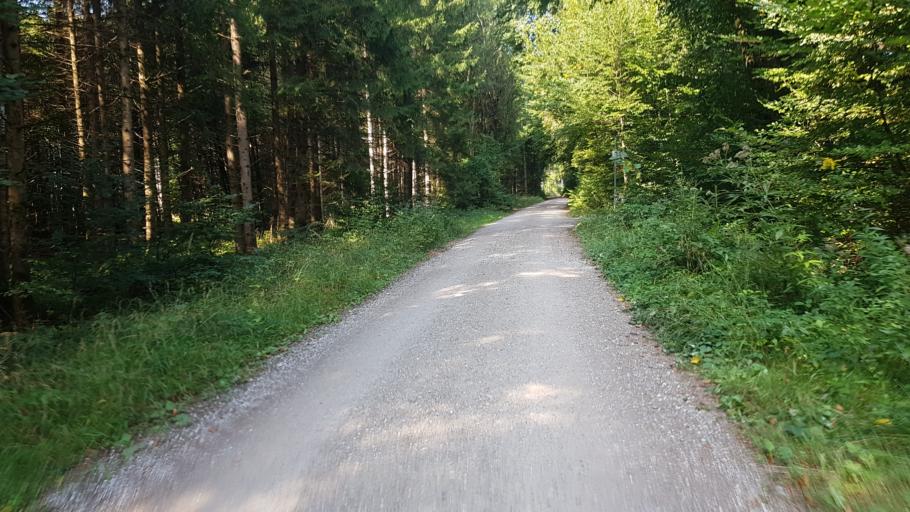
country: DE
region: Bavaria
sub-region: Upper Bavaria
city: Gilching
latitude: 48.0797
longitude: 11.3104
